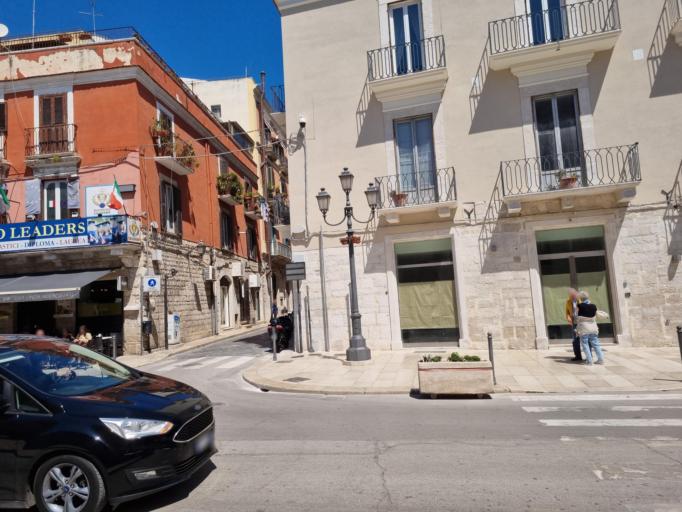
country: IT
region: Apulia
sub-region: Provincia di Barletta - Andria - Trani
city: Barletta
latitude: 41.3192
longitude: 16.2818
